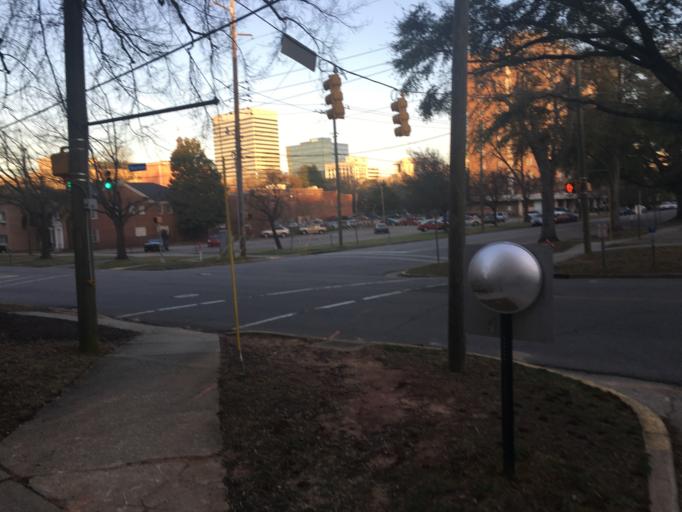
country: US
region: South Carolina
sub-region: Richland County
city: Columbia
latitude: 33.9994
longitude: -81.0288
